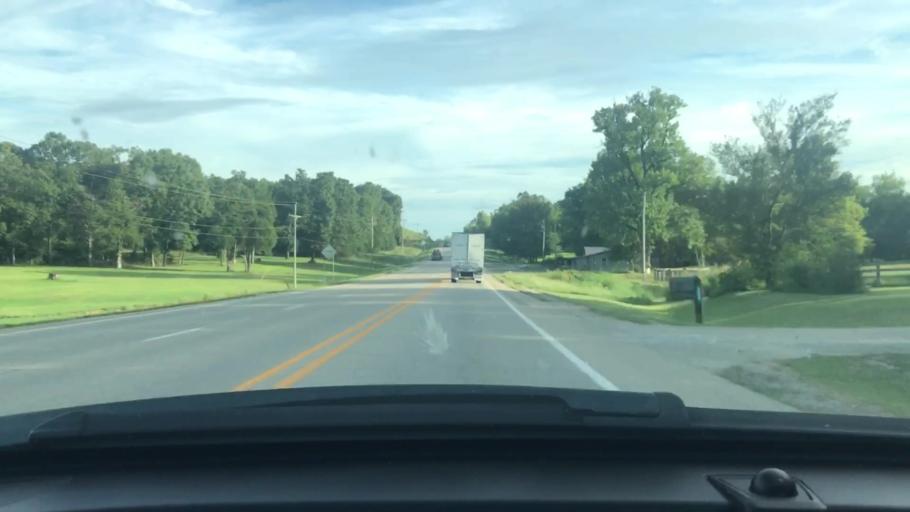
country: US
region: Arkansas
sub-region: Lawrence County
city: Hoxie
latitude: 36.1525
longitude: -91.1610
